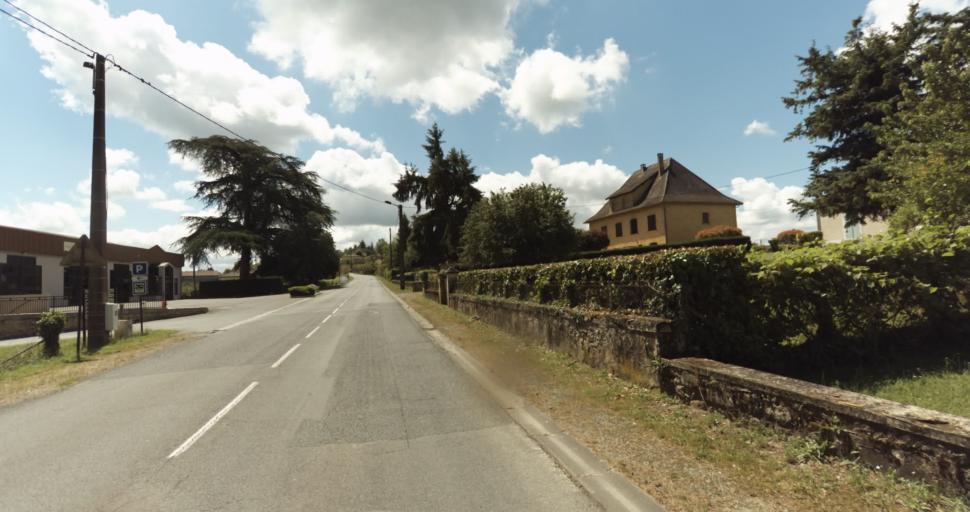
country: FR
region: Aquitaine
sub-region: Departement de la Dordogne
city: Beaumont-du-Perigord
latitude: 44.7750
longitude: 0.7647
